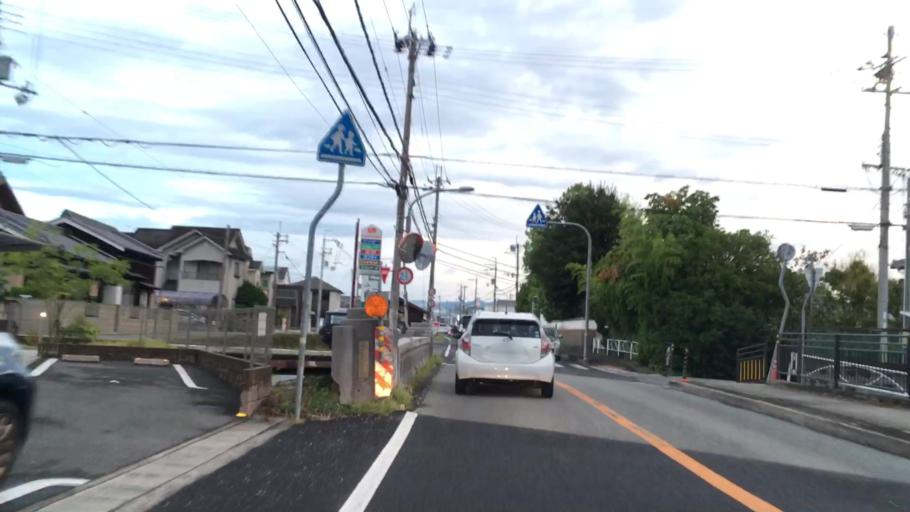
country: JP
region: Hyogo
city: Himeji
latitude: 34.9039
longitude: 134.7363
